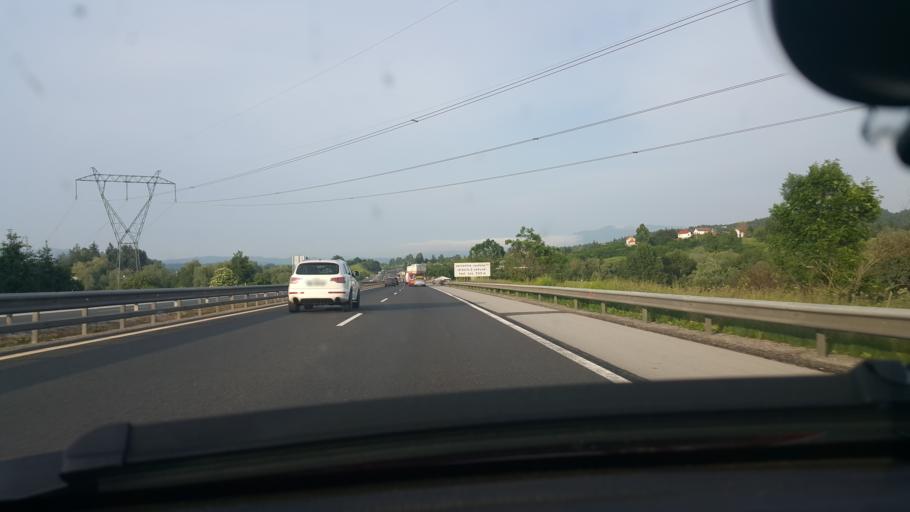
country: SI
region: Postojna
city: Postojna
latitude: 45.7603
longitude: 14.0970
